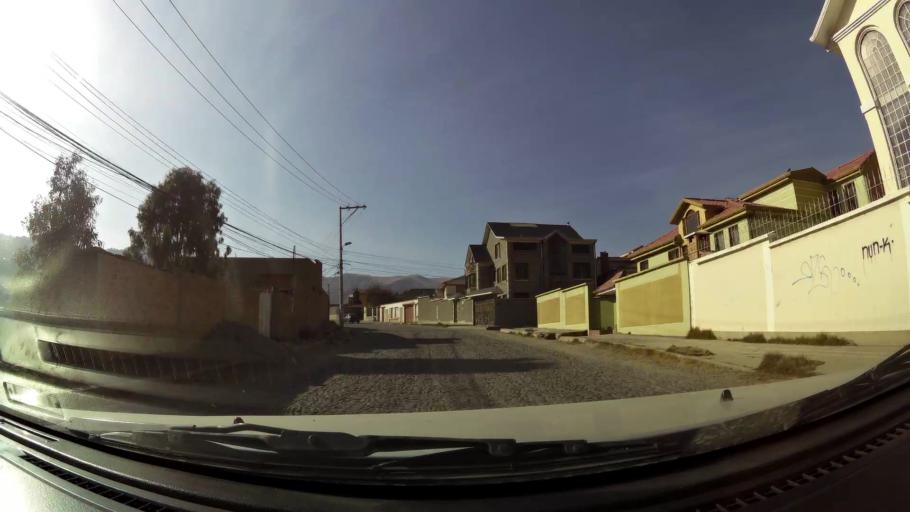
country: BO
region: La Paz
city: La Paz
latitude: -16.5131
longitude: -68.0841
